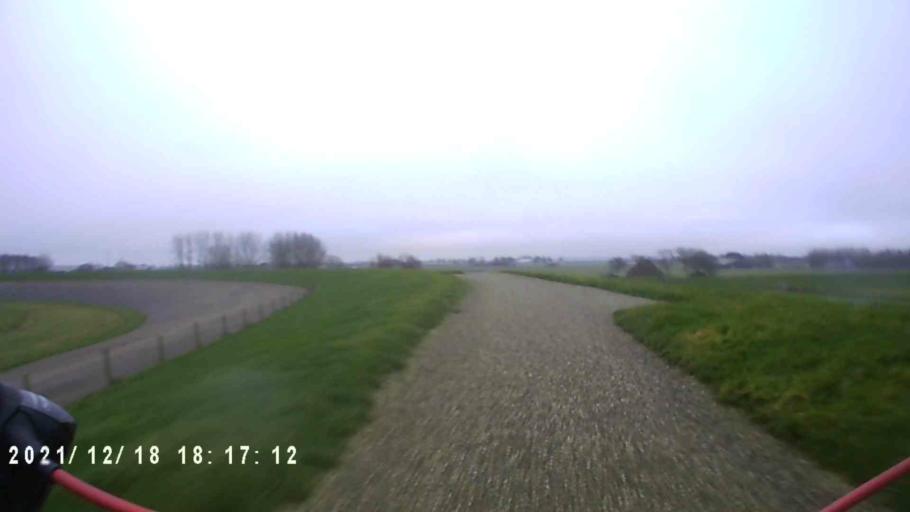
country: NL
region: Friesland
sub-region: Gemeente Dongeradeel
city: Ternaard
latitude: 53.3929
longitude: 5.9706
